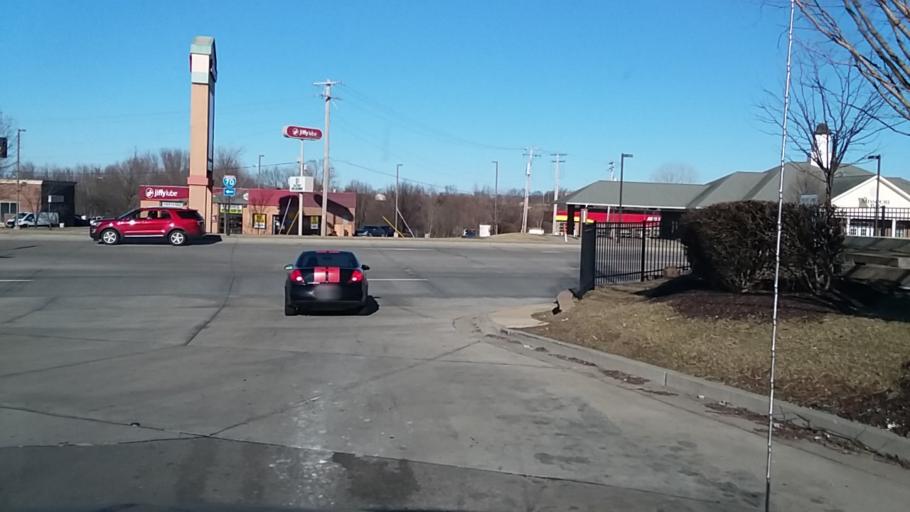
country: US
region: Missouri
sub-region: Saint Charles County
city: Wentzville
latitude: 38.8123
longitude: -90.8735
